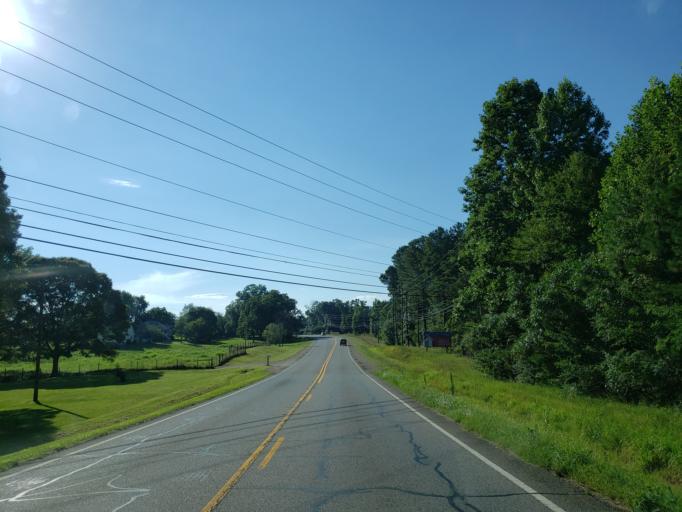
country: US
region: Georgia
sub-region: Cherokee County
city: Ball Ground
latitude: 34.2505
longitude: -84.3099
